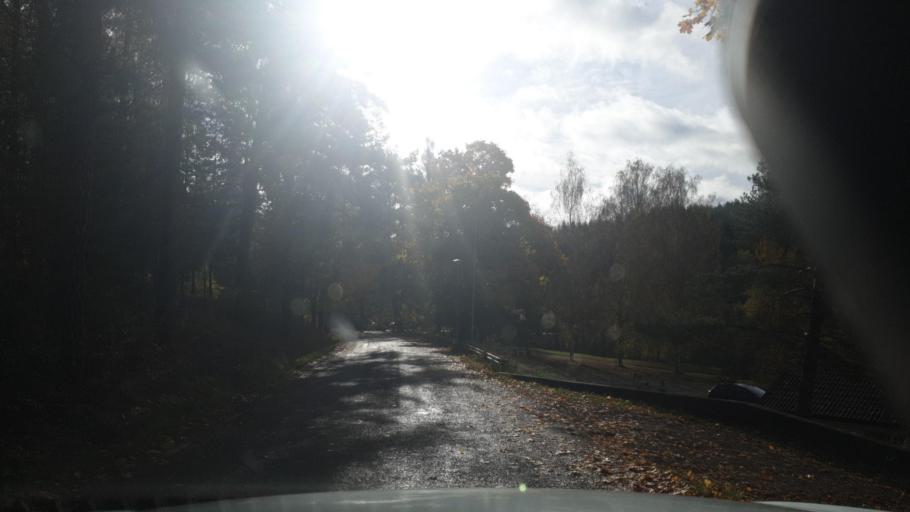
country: SE
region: Vaermland
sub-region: Sunne Kommun
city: Sunne
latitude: 59.6196
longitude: 12.9609
